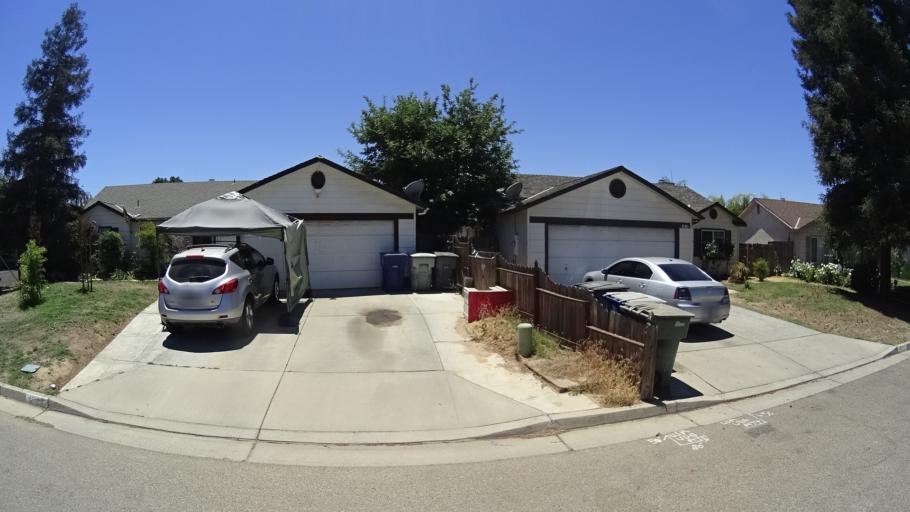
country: US
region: California
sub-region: Fresno County
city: Fresno
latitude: 36.7909
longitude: -119.8133
